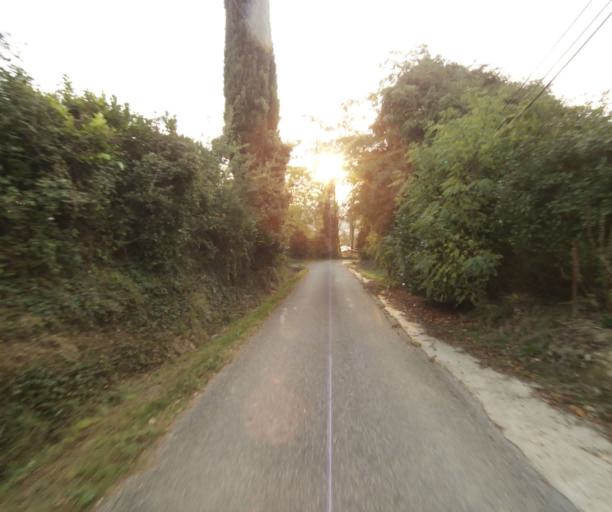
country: FR
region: Midi-Pyrenees
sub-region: Departement du Tarn-et-Garonne
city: Grisolles
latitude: 43.8303
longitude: 1.3076
